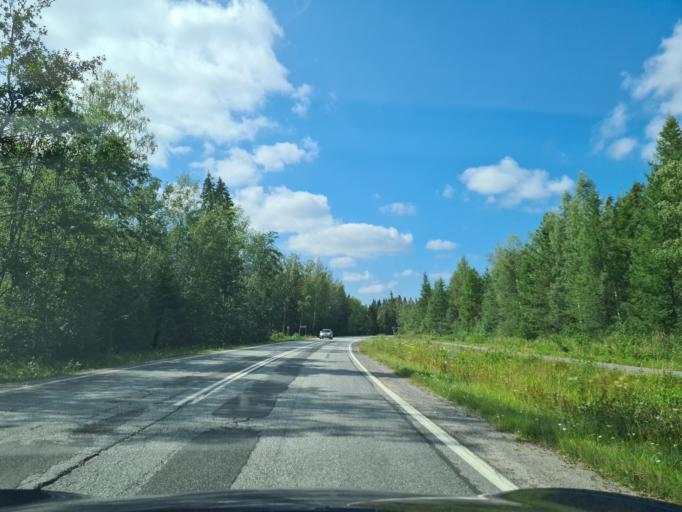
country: FI
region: Ostrobothnia
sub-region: Vaasa
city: Vaasa
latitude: 63.1949
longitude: 21.5506
